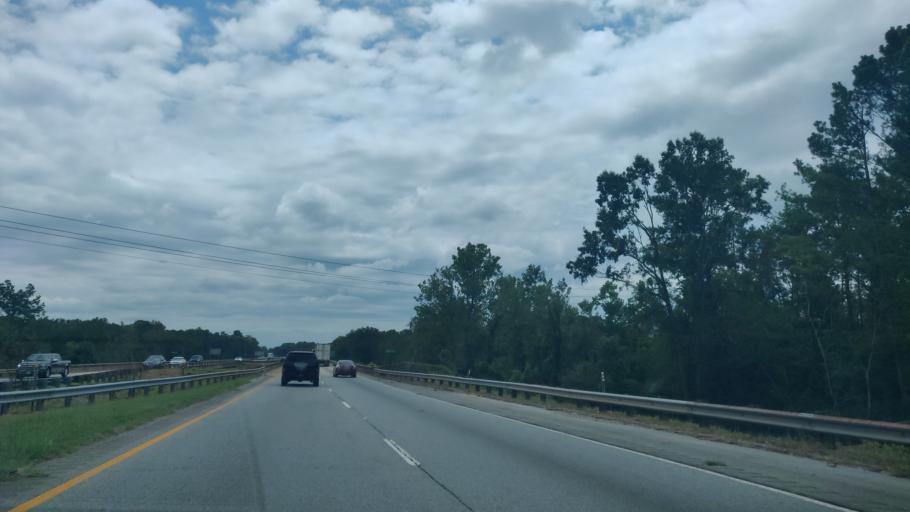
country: US
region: Georgia
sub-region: Dougherty County
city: Albany
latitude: 31.6011
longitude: -84.1466
